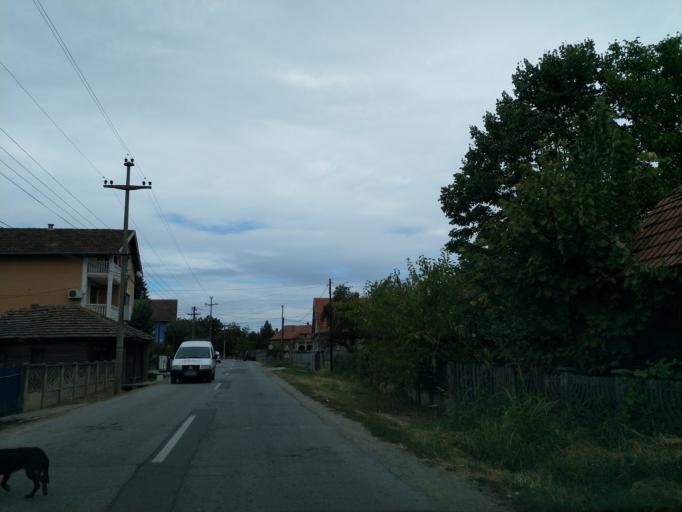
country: RS
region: Central Serbia
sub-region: Pomoravski Okrug
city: Paracin
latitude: 43.8359
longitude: 21.3219
